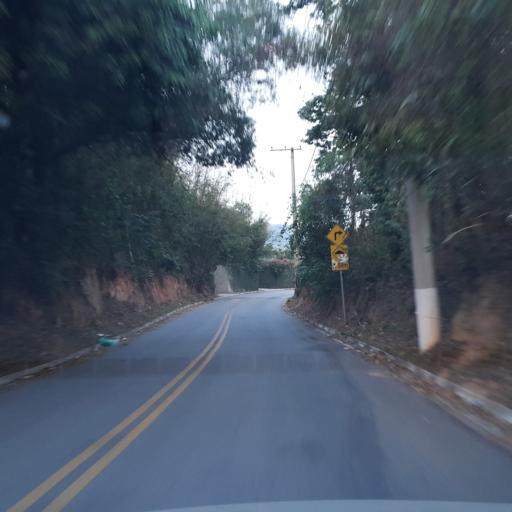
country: BR
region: Sao Paulo
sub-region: Louveira
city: Louveira
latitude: -23.0643
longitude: -46.9666
